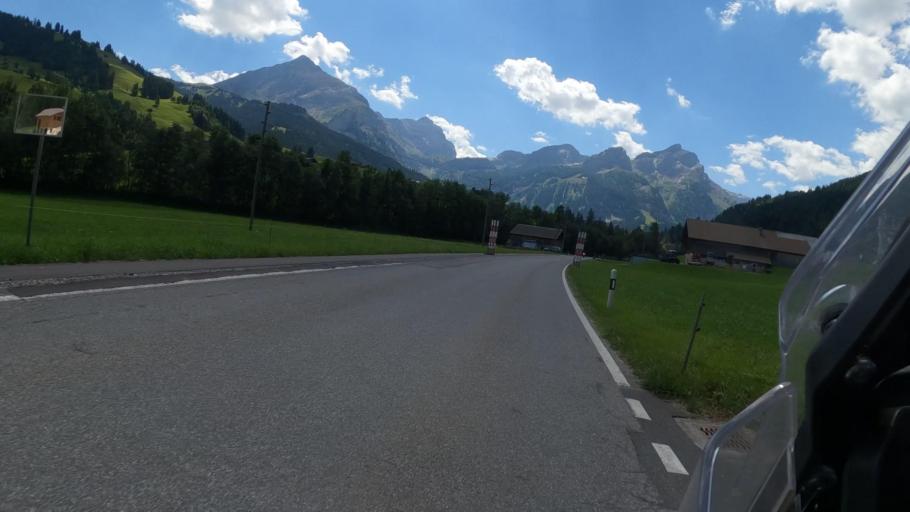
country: CH
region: Bern
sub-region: Obersimmental-Saanen District
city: Gstaad
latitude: 46.4056
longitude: 7.2685
